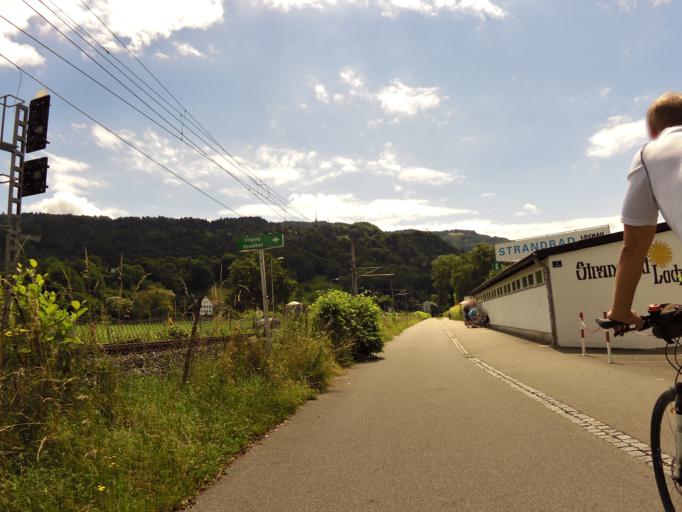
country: AT
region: Vorarlberg
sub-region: Politischer Bezirk Bregenz
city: Lochau
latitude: 47.5254
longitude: 9.7472
